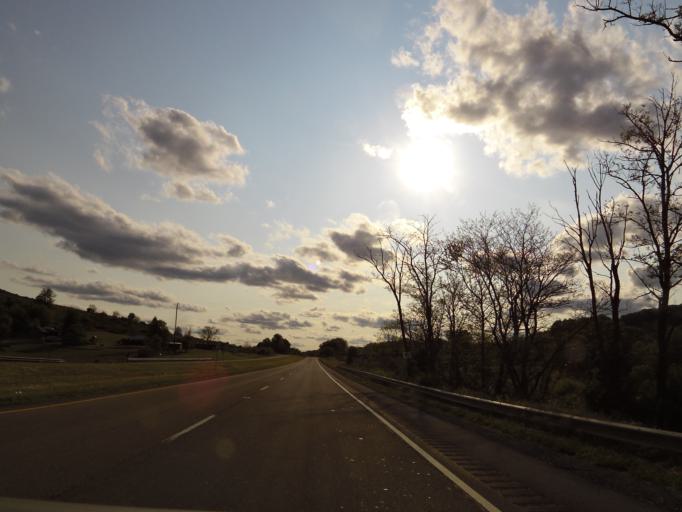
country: US
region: Virginia
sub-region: Tazewell County
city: Tazewell
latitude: 37.1199
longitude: -81.5791
